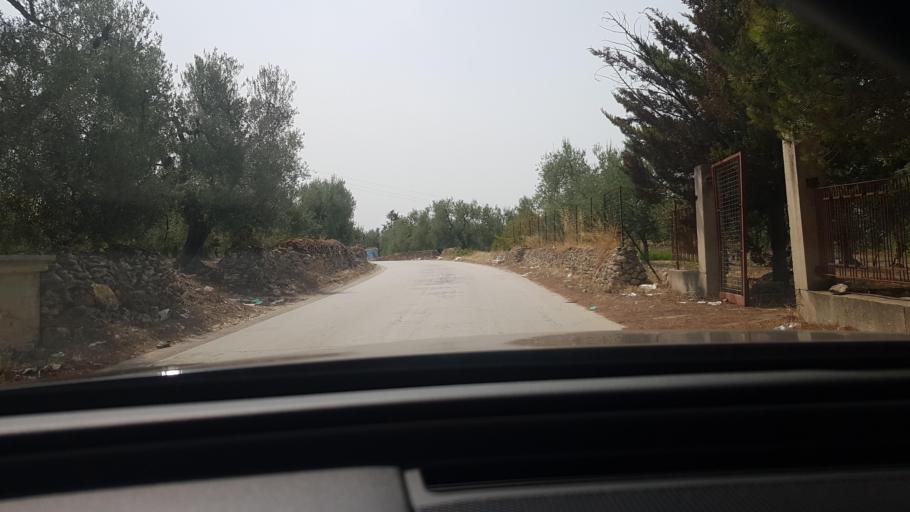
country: IT
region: Apulia
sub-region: Provincia di Barletta - Andria - Trani
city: Andria
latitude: 41.2272
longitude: 16.2683
